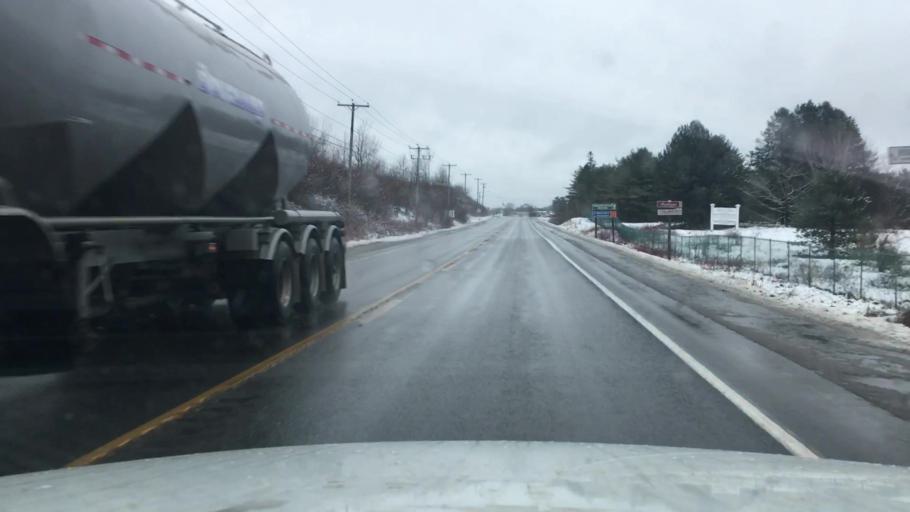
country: US
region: Maine
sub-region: Knox County
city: Thomaston
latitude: 44.0901
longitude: -69.1497
